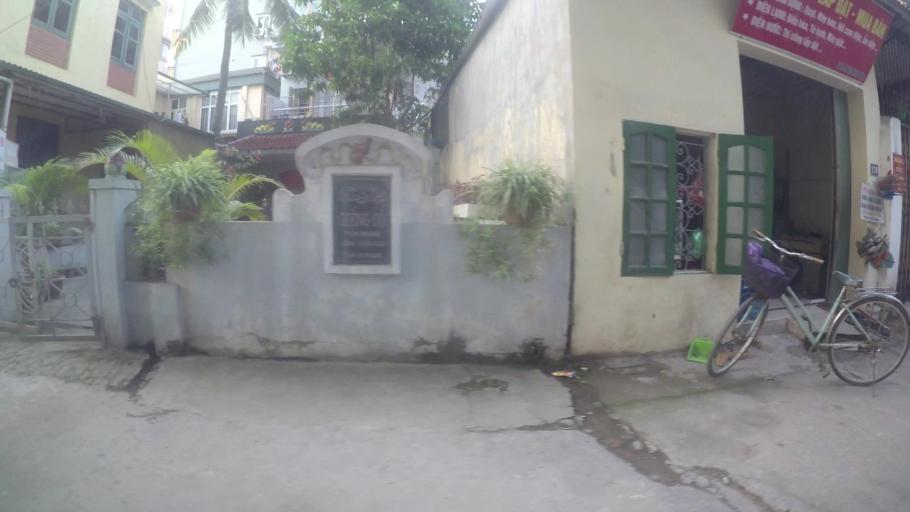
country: VN
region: Ha Noi
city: Tay Ho
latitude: 21.0675
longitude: 105.7914
